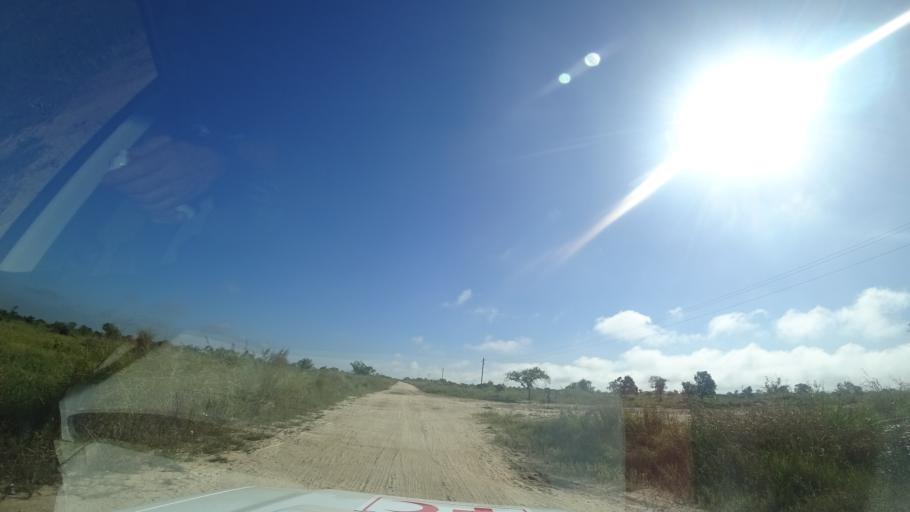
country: MZ
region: Sofala
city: Dondo
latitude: -19.4446
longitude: 34.5620
